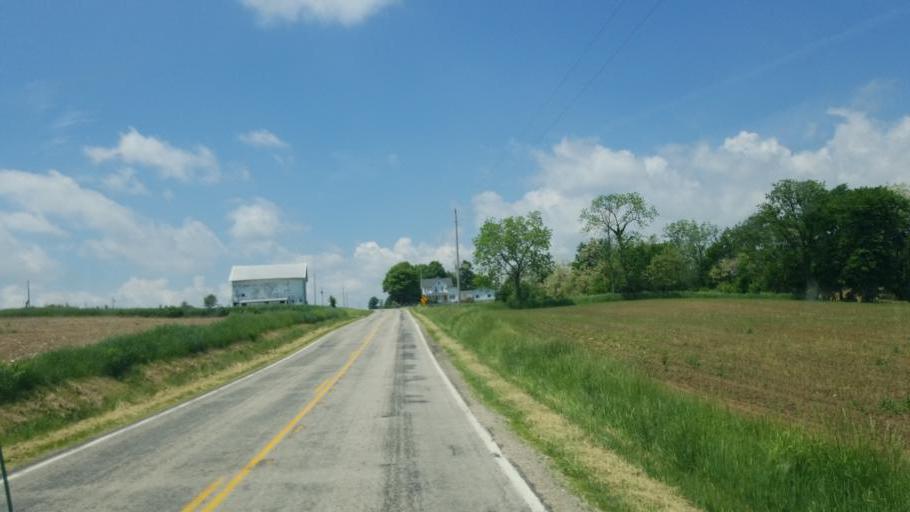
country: US
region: Ohio
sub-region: Ashland County
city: Ashland
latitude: 40.8188
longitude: -82.2555
